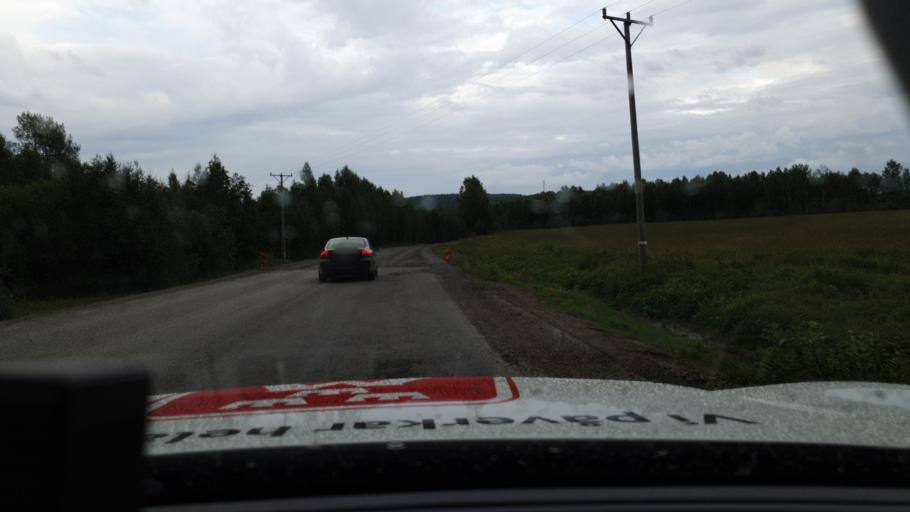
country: SE
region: Norrbotten
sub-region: Bodens Kommun
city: Boden
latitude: 65.8507
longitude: 21.5749
